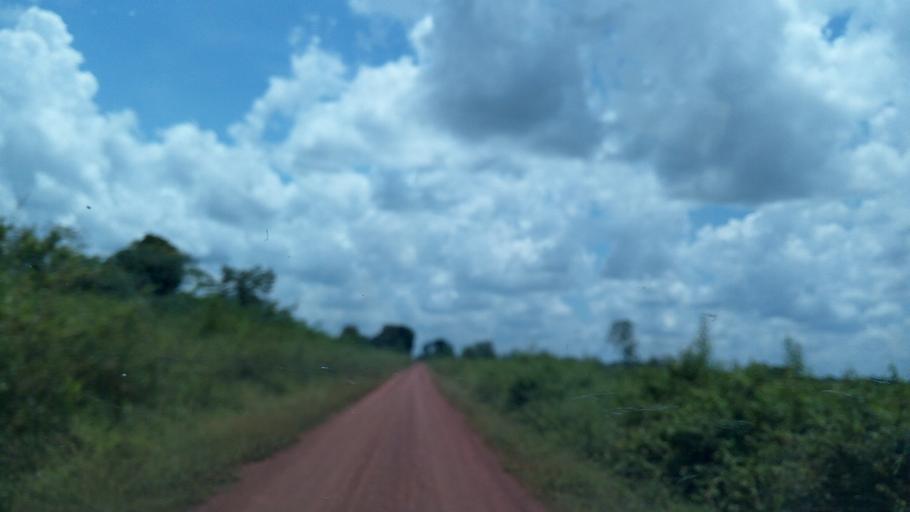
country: CD
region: Equateur
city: Libenge
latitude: 3.7726
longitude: 18.9448
